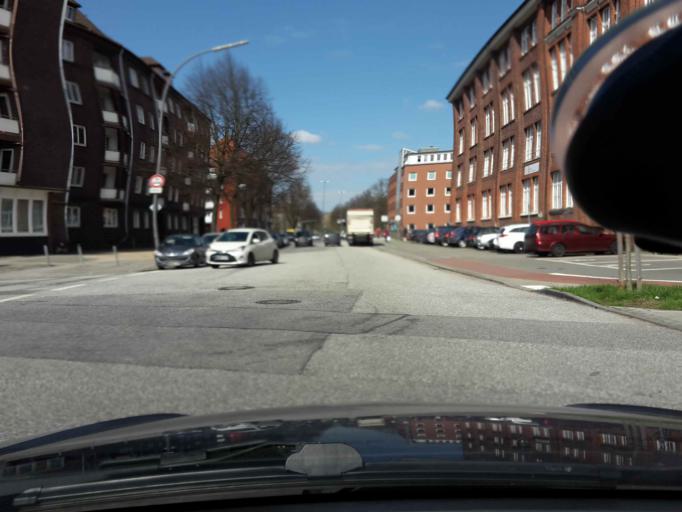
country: DE
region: Hamburg
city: Rothenburgsort
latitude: 53.5492
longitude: 10.0595
